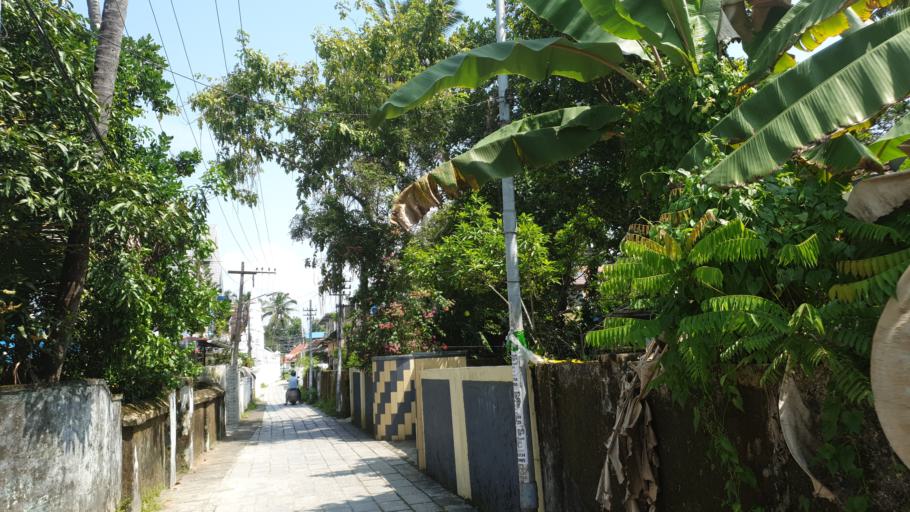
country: IN
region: Kerala
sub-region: Ernakulam
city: Cochin
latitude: 9.9730
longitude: 76.2423
